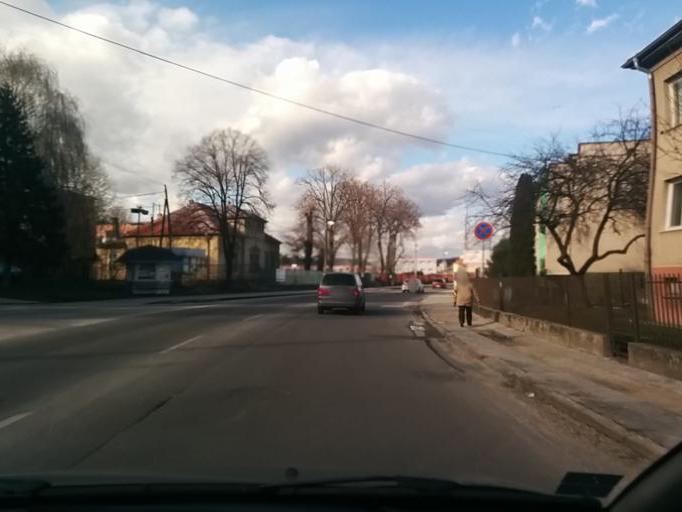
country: SK
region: Trenciansky
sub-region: Okres Nove Mesto nad Vahom
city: Nove Mesto nad Vahom
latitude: 48.7626
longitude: 17.8339
